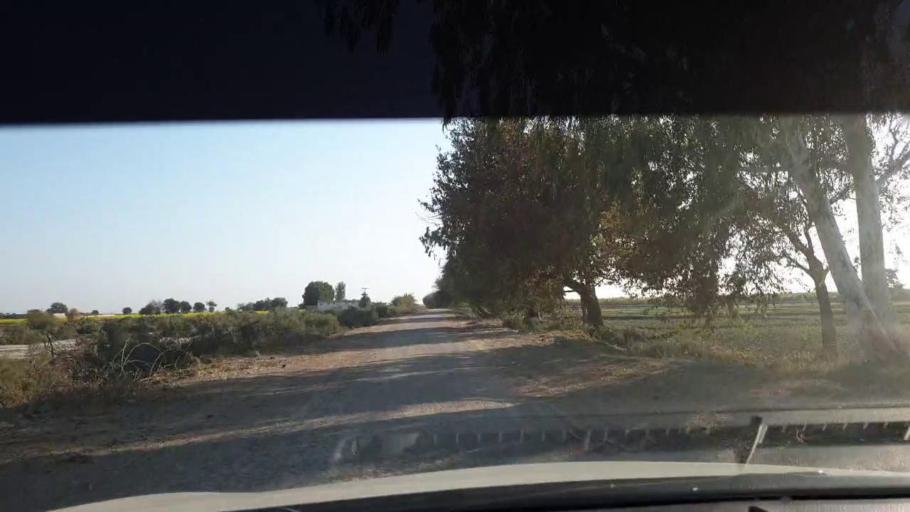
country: PK
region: Sindh
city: Berani
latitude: 25.7987
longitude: 68.9260
